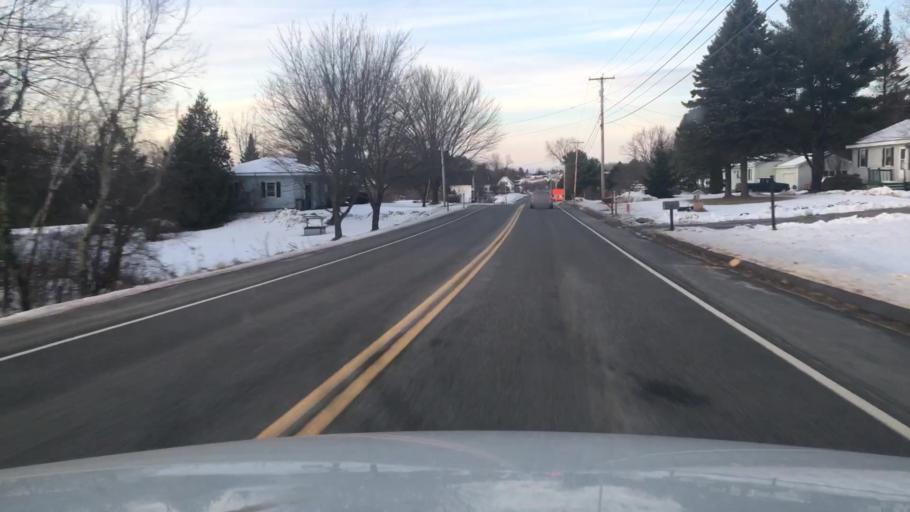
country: US
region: Maine
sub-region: Androscoggin County
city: Sabattus
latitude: 44.0962
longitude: -70.0841
